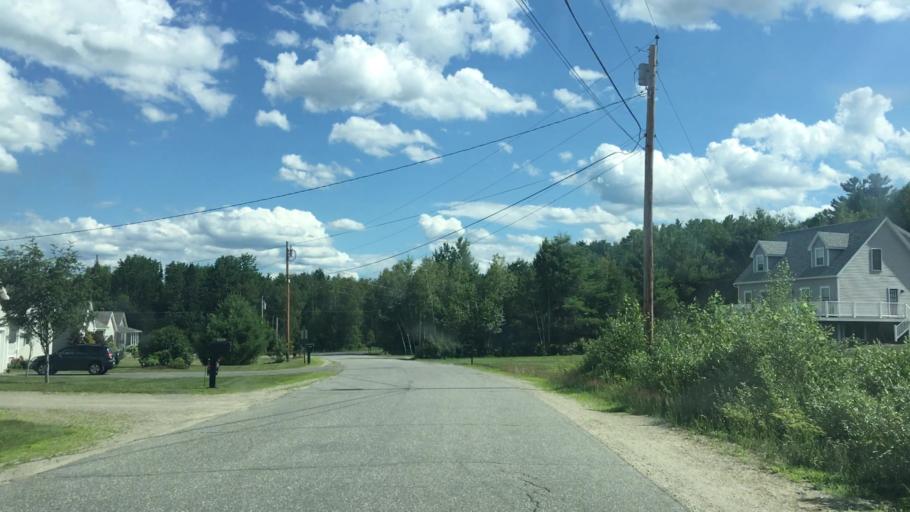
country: US
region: Maine
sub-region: Franklin County
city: Farmington
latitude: 44.6694
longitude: -70.1308
